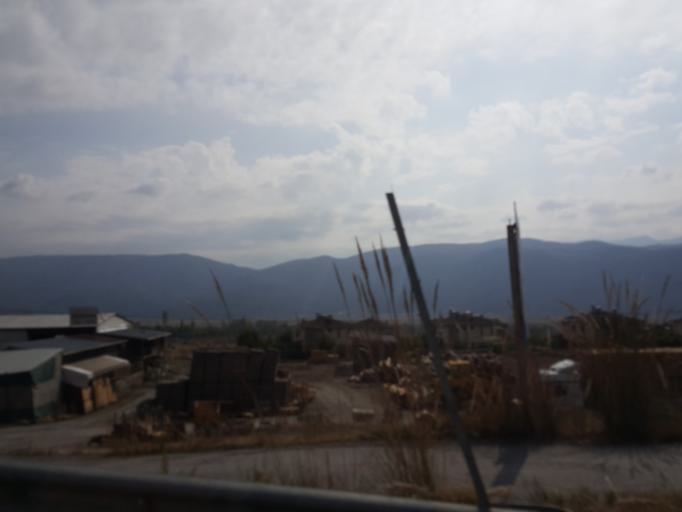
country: TR
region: Corum
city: Kargi
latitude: 41.1349
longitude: 34.4634
